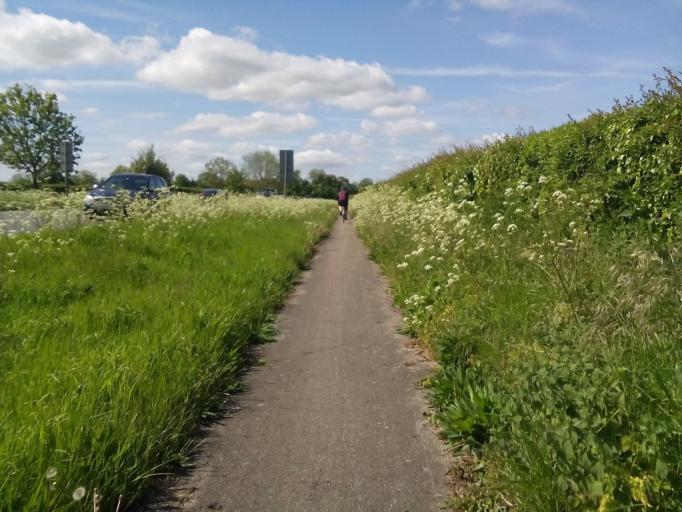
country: GB
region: England
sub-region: Cambridgeshire
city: Harston
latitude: 52.1325
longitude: 0.0721
